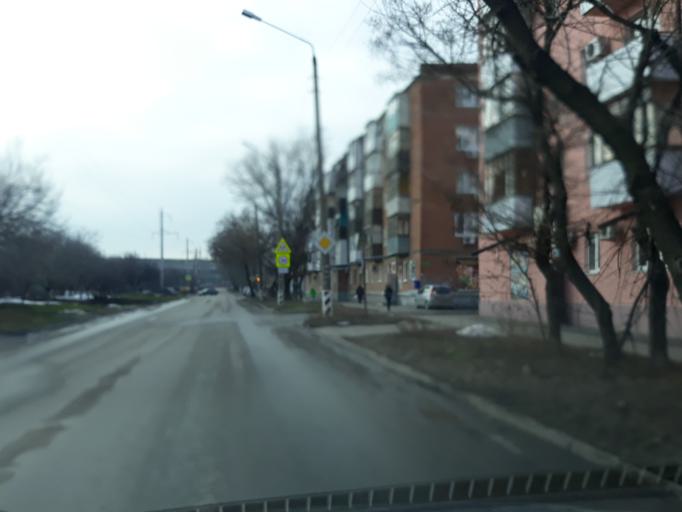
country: RU
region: Rostov
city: Taganrog
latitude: 47.2500
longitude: 38.9112
